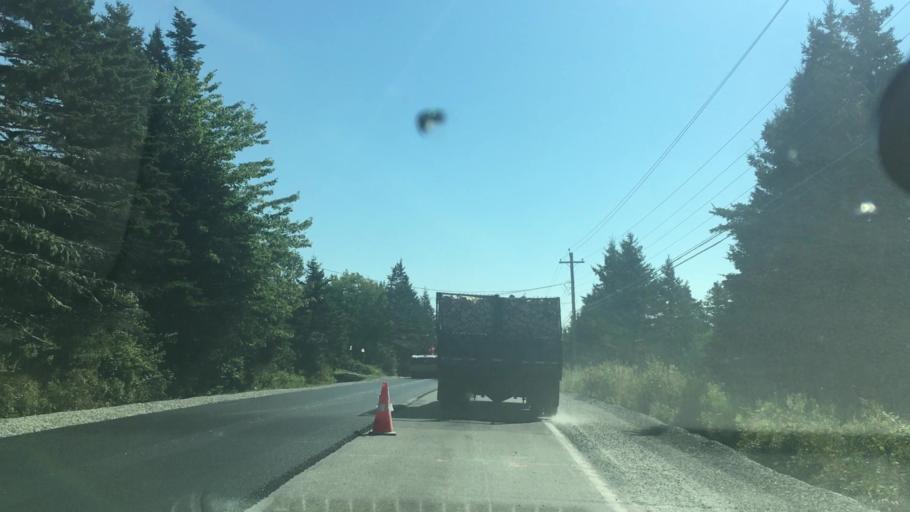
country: CA
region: Nova Scotia
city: New Glasgow
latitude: 44.9088
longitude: -62.5005
